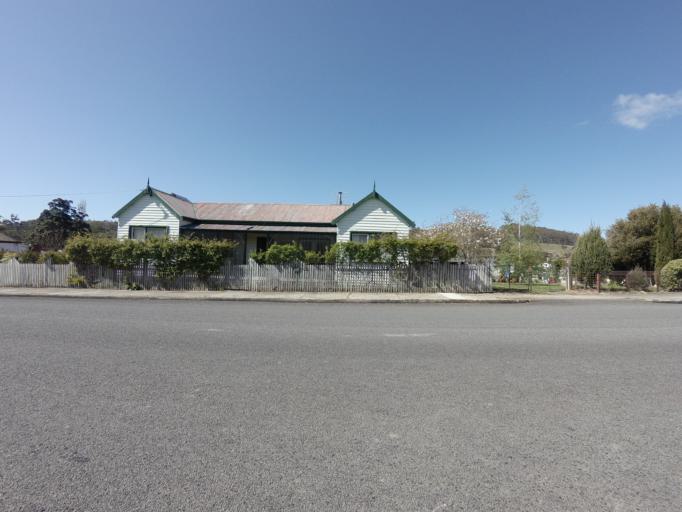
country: AU
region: Tasmania
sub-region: Derwent Valley
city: New Norfolk
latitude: -42.6172
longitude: 146.7159
